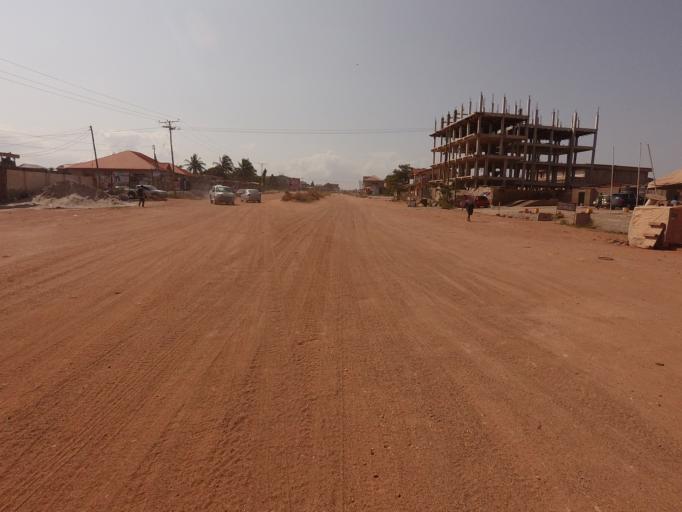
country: GH
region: Greater Accra
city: Teshi Old Town
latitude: 5.6041
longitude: -0.1216
